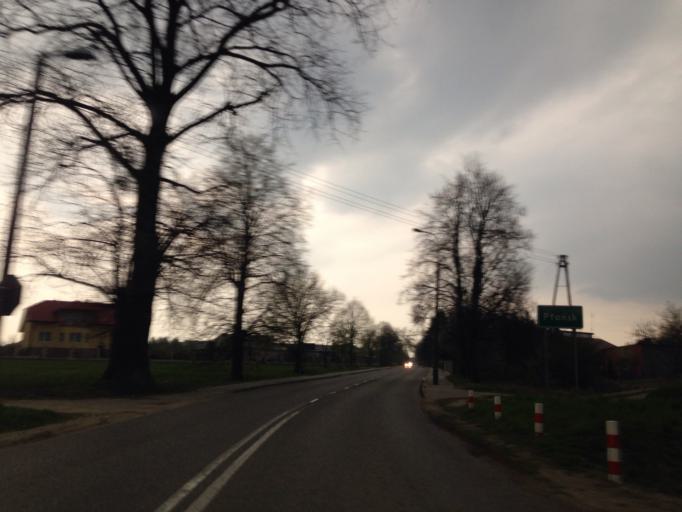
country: PL
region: Masovian Voivodeship
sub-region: Powiat plonski
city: Plonsk
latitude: 52.6371
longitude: 20.3543
